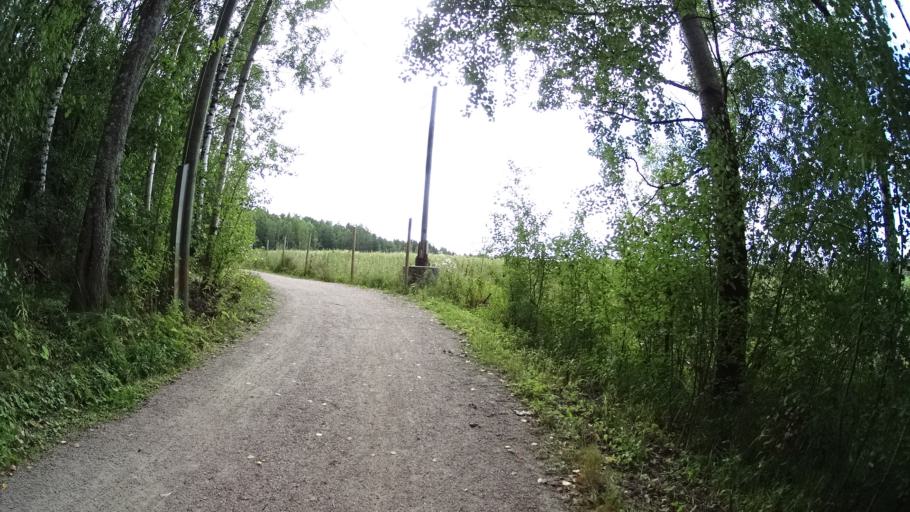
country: FI
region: Uusimaa
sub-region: Helsinki
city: Teekkarikylae
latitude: 60.2638
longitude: 24.9002
